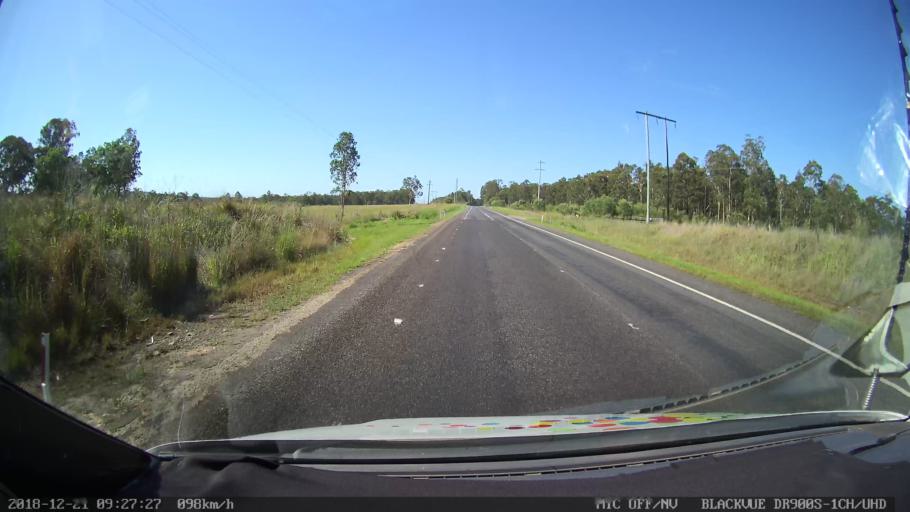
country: AU
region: New South Wales
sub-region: Clarence Valley
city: Maclean
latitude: -29.4029
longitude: 152.9900
